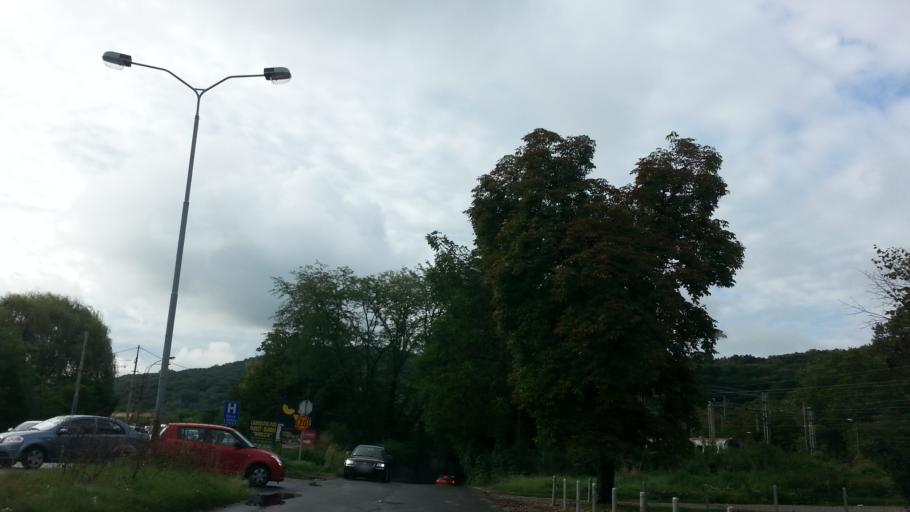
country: RS
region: Central Serbia
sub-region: Belgrade
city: Savski Venac
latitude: 44.7732
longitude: 20.4377
